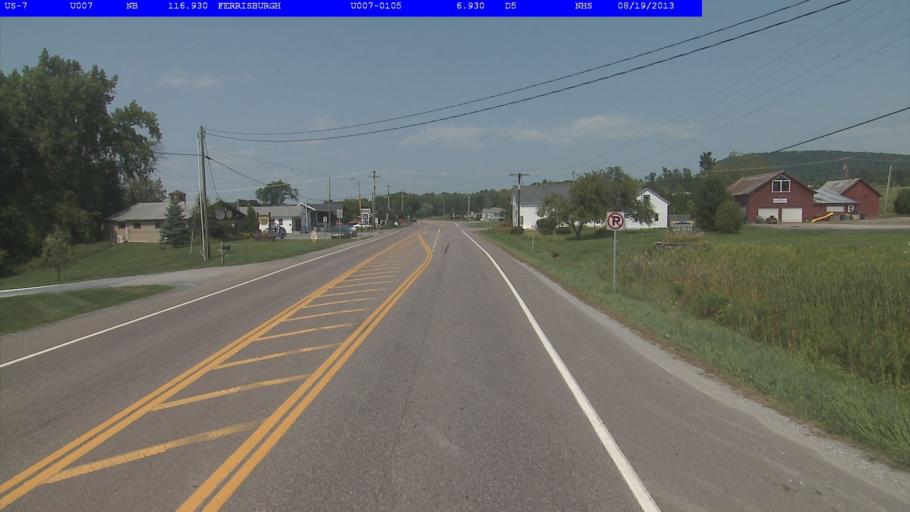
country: US
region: Vermont
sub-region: Addison County
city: Vergennes
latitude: 44.2577
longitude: -73.2281
